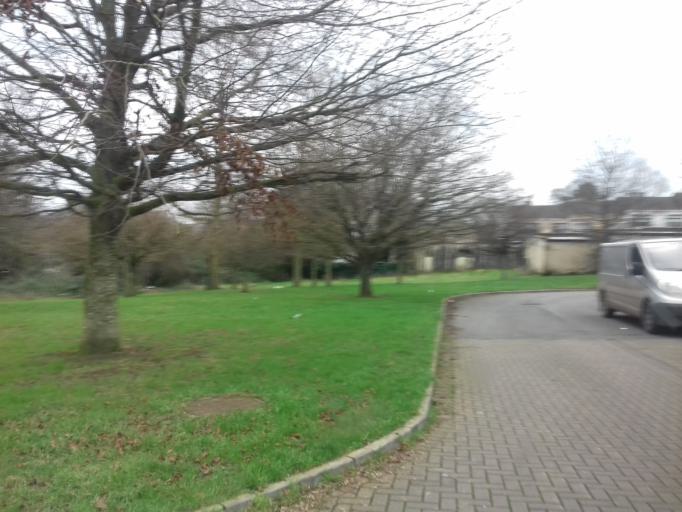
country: IE
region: Leinster
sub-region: An Mhi
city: Duleek
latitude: 53.6908
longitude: -6.4194
